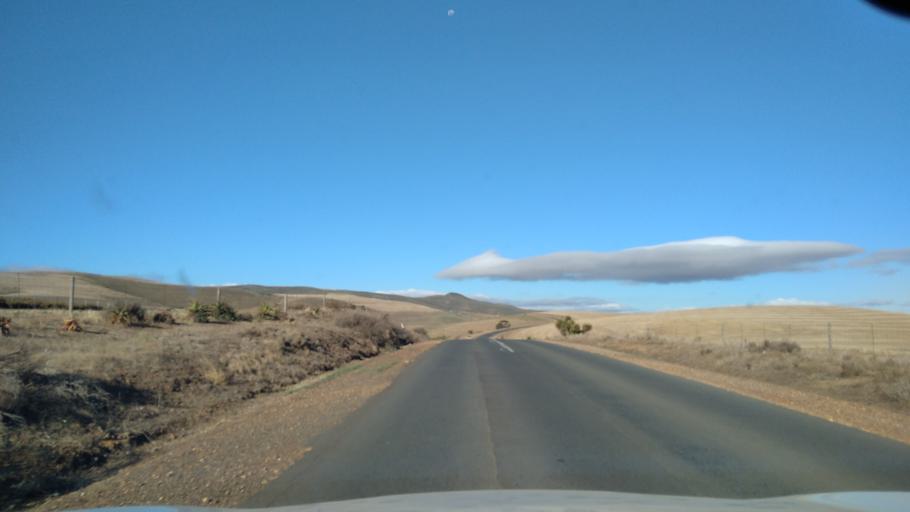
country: ZA
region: Western Cape
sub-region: Overberg District Municipality
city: Caledon
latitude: -34.1693
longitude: 19.2893
